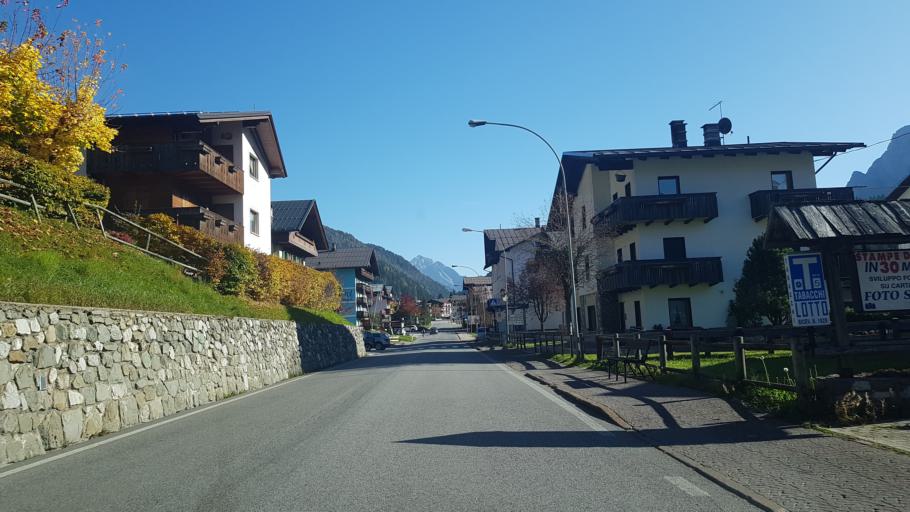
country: IT
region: Veneto
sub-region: Provincia di Belluno
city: Granvilla
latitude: 46.5678
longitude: 12.6954
